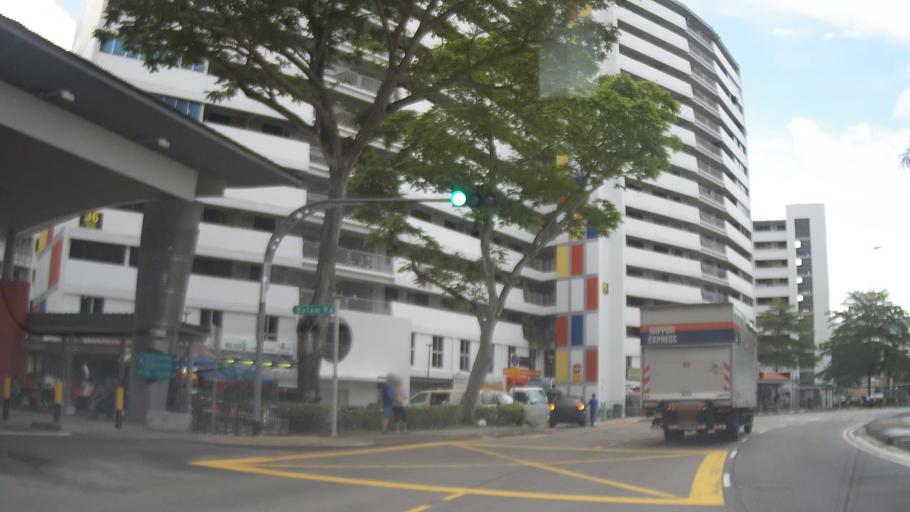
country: SG
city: Singapore
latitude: 1.3289
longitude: 103.8863
